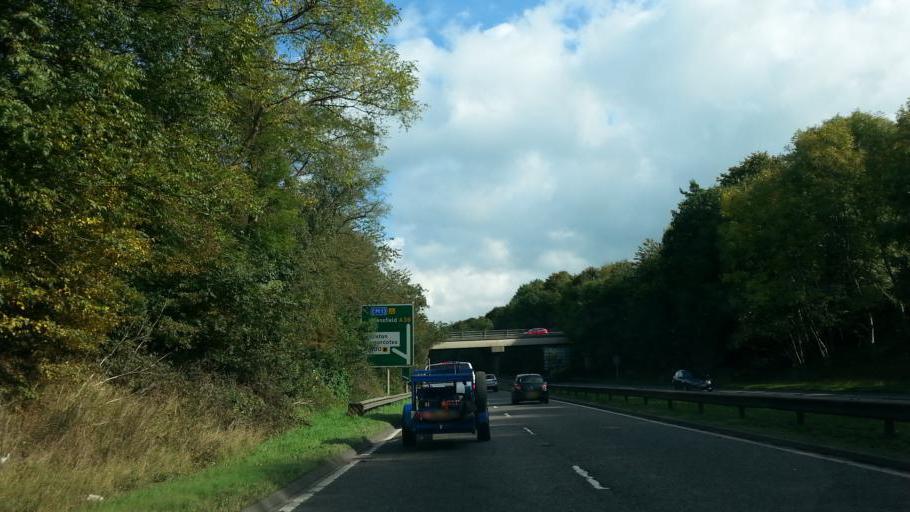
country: GB
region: England
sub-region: Derbyshire
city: Alfreton
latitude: 53.0909
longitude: -1.3779
